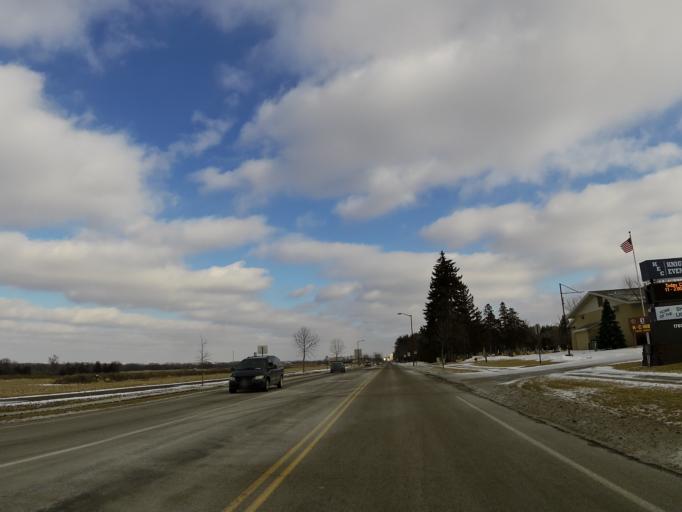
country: US
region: Minnesota
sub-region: Scott County
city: Shakopee
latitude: 44.7973
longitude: -93.5003
